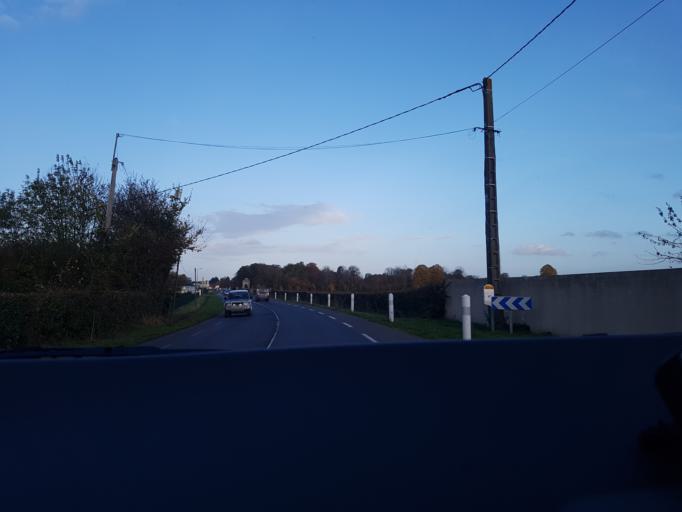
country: FR
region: Lower Normandy
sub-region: Departement du Calvados
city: Sannerville
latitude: 49.1748
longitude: -0.2357
